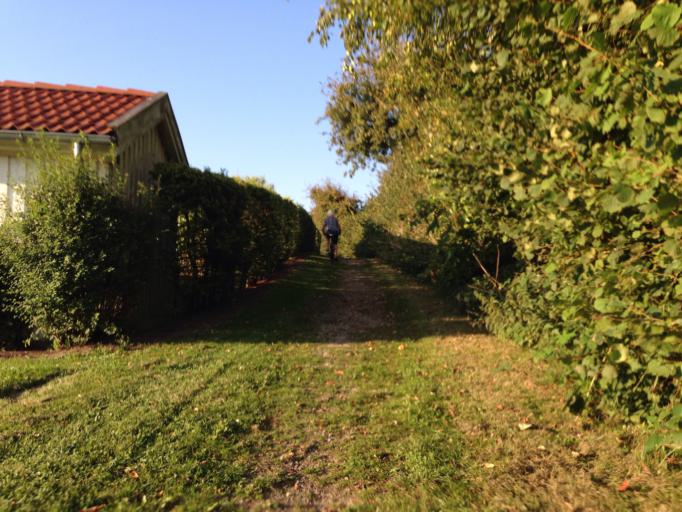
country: DK
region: South Denmark
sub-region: Middelfart Kommune
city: Norre Aby
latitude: 55.4882
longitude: 9.9157
